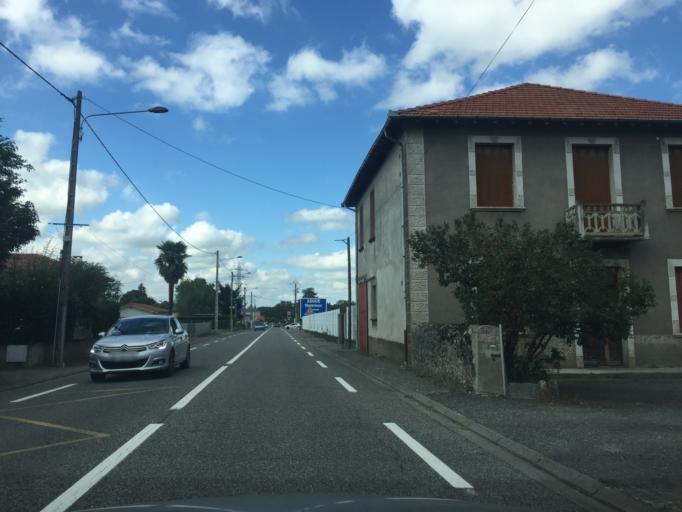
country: FR
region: Midi-Pyrenees
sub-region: Departement de la Haute-Garonne
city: Gourdan-Polignan
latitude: 43.0724
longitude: 0.5857
